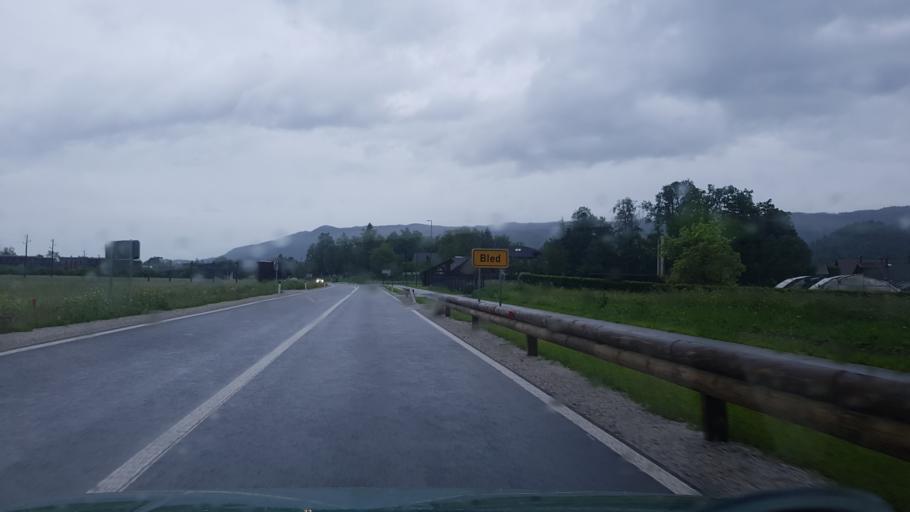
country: SI
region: Bled
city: Bled
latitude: 46.3744
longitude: 14.1121
